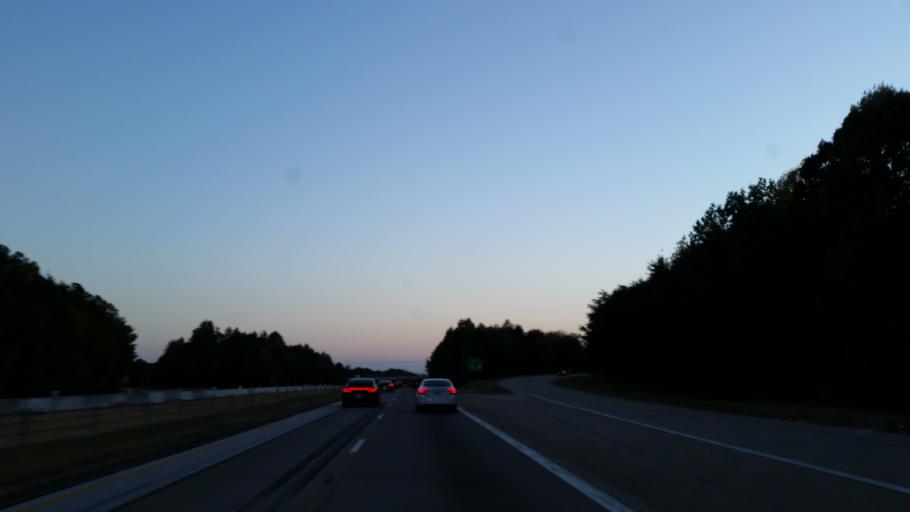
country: US
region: Georgia
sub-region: Forsyth County
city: Cumming
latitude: 34.2333
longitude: -84.1004
